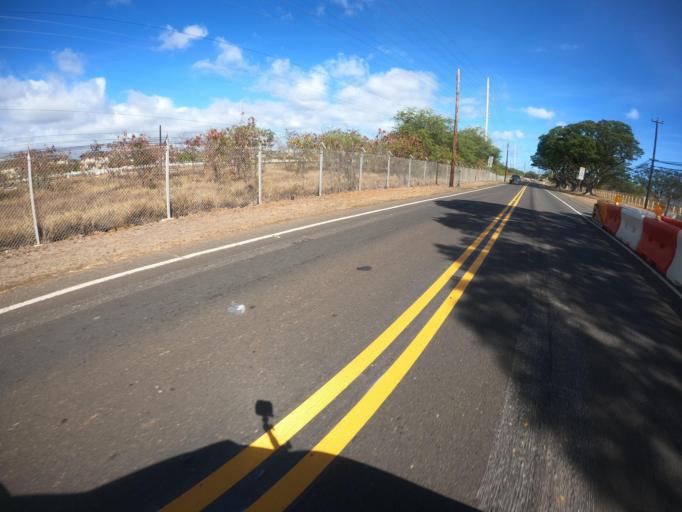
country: US
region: Hawaii
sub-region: Honolulu County
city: Makakilo City
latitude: 21.3240
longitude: -158.0818
